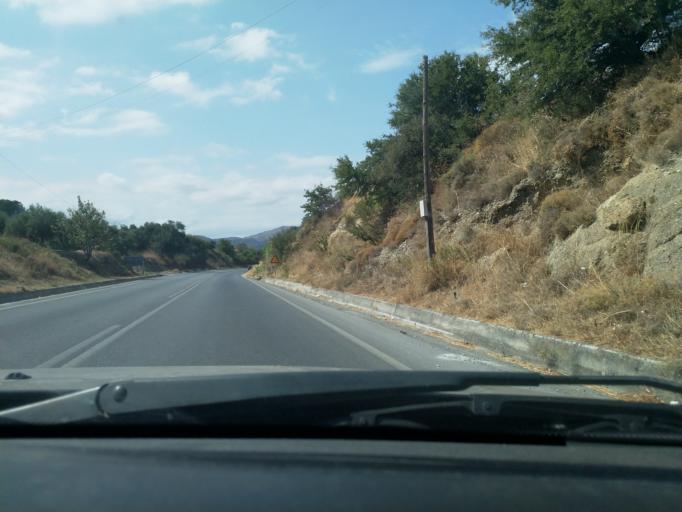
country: GR
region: Crete
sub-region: Nomos Rethymnis
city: Atsipopoulon
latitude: 35.2267
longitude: 24.4777
